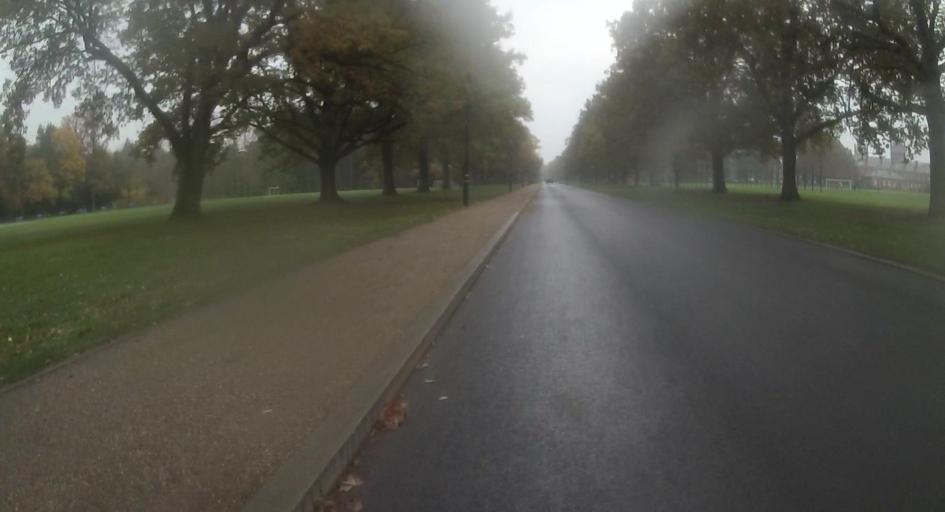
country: GB
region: England
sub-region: Bracknell Forest
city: Crowthorne
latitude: 51.3670
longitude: -0.8097
